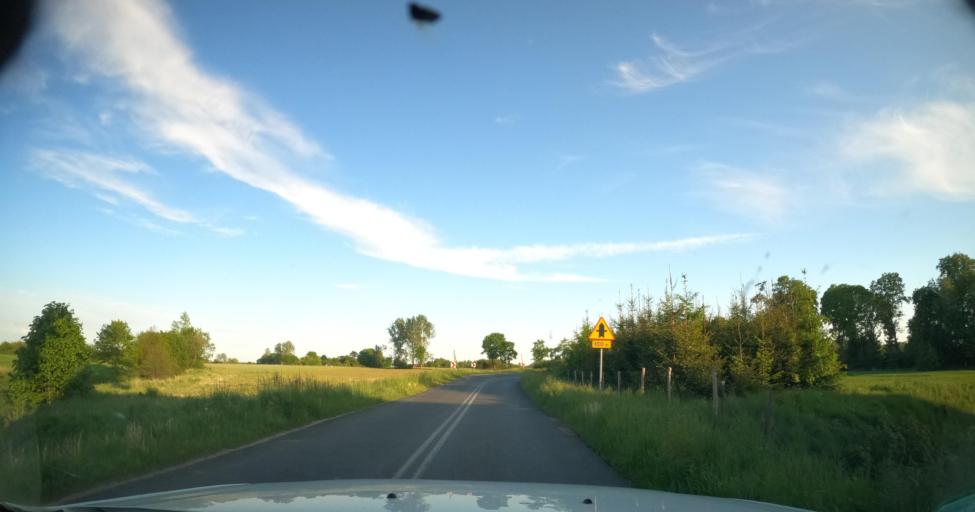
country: PL
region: Warmian-Masurian Voivodeship
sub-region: Powiat lidzbarski
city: Orneta
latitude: 54.1757
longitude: 20.1591
